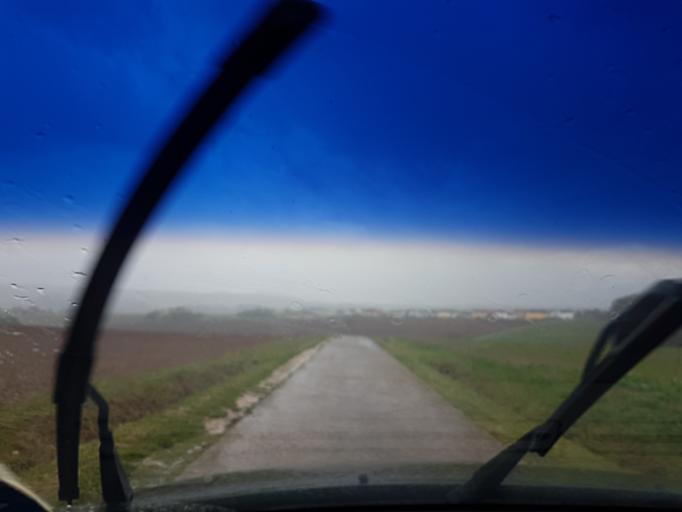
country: DE
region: Bavaria
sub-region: Regierungsbezirk Mittelfranken
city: Burghaslach
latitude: 49.7435
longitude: 10.6089
